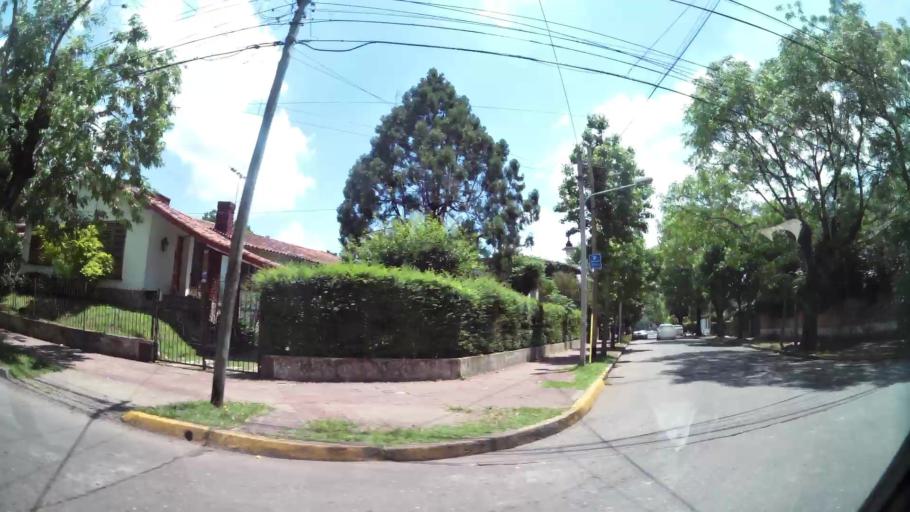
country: AR
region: Buenos Aires
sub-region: Partido de Tigre
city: Tigre
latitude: -34.4168
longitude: -58.5872
